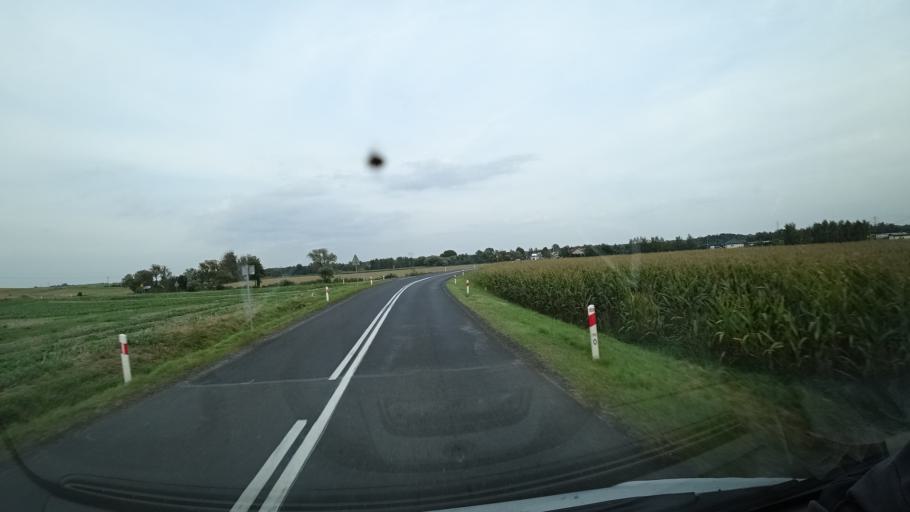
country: PL
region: Silesian Voivodeship
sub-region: Powiat gliwicki
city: Toszek
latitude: 50.3988
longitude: 18.4763
